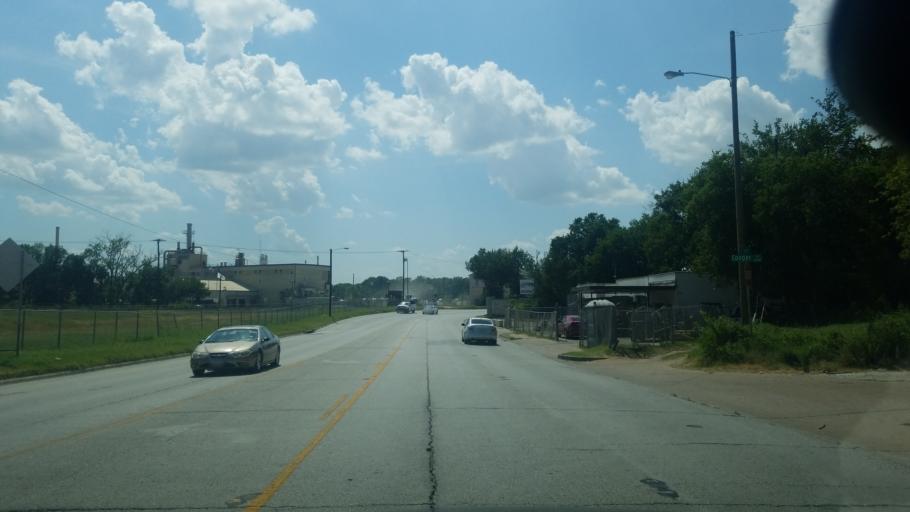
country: US
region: Texas
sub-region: Dallas County
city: Dallas
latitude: 32.7548
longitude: -96.7759
